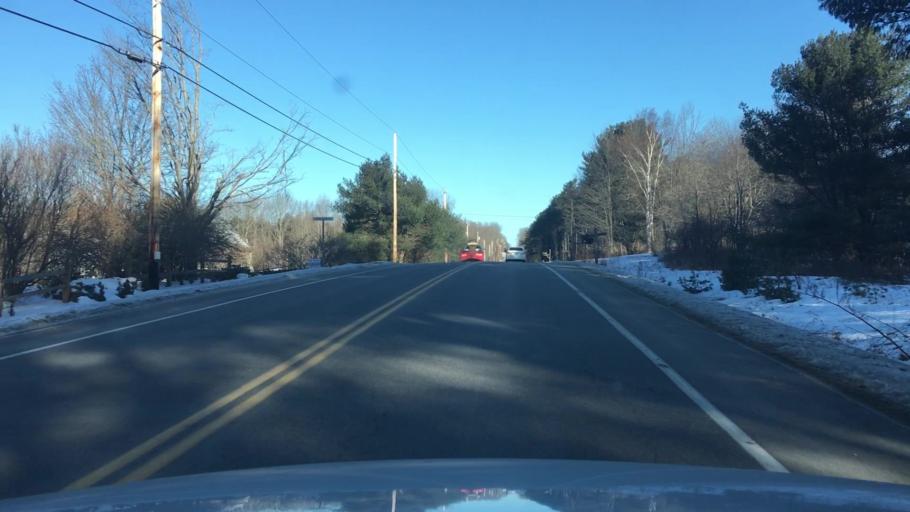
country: US
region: Maine
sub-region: Cumberland County
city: Freeport
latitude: 43.9037
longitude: -70.1166
